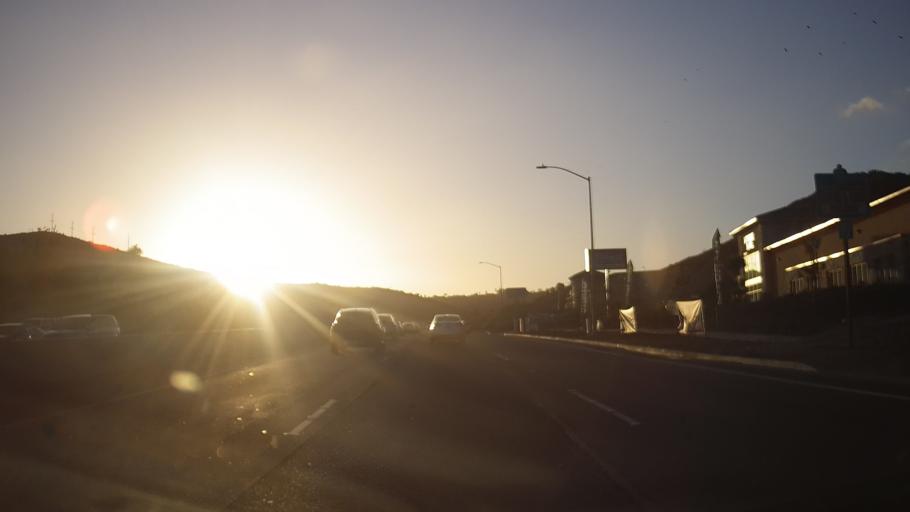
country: US
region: California
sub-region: San Diego County
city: Rancho San Diego
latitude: 32.7390
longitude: -116.9438
